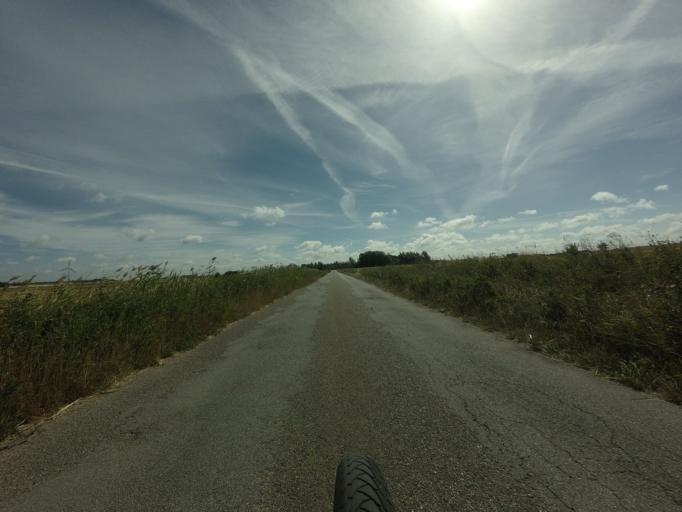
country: DK
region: North Denmark
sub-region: Hjorring Kommune
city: Vra
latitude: 57.3406
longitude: 9.8043
